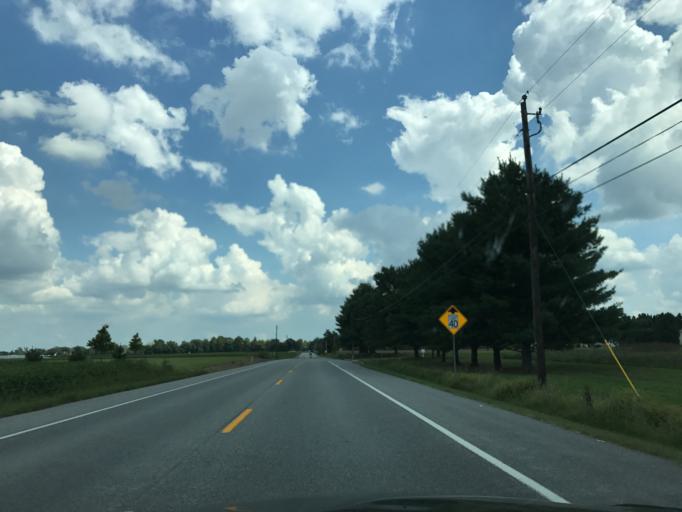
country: US
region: Maryland
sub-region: Queen Anne's County
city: Kingstown
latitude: 39.1857
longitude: -75.8732
